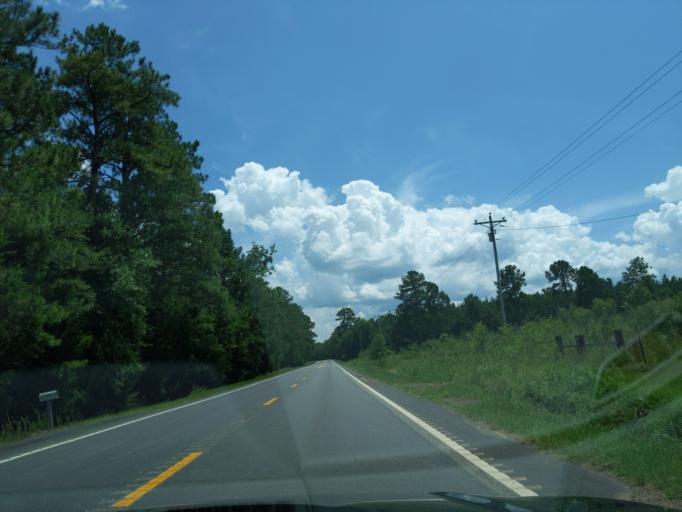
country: US
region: South Carolina
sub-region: Edgefield County
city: Edgefield
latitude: 33.8558
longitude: -81.9828
